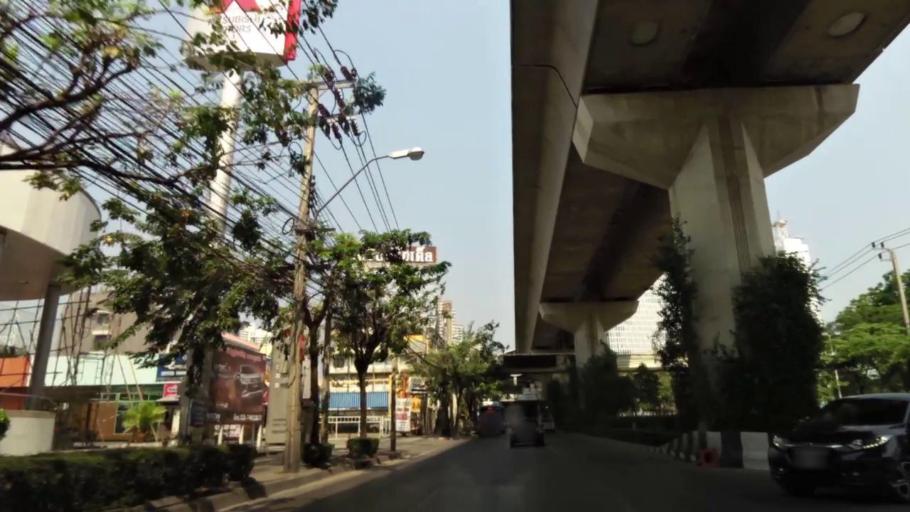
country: TH
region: Bangkok
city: Phra Khanong
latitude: 13.6665
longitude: 100.6039
